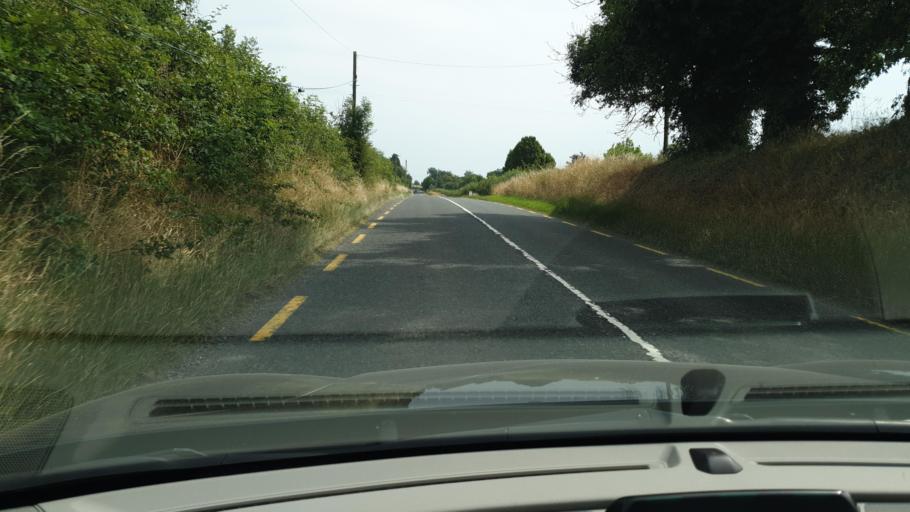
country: IE
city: Kentstown
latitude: 53.6362
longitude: -6.5967
